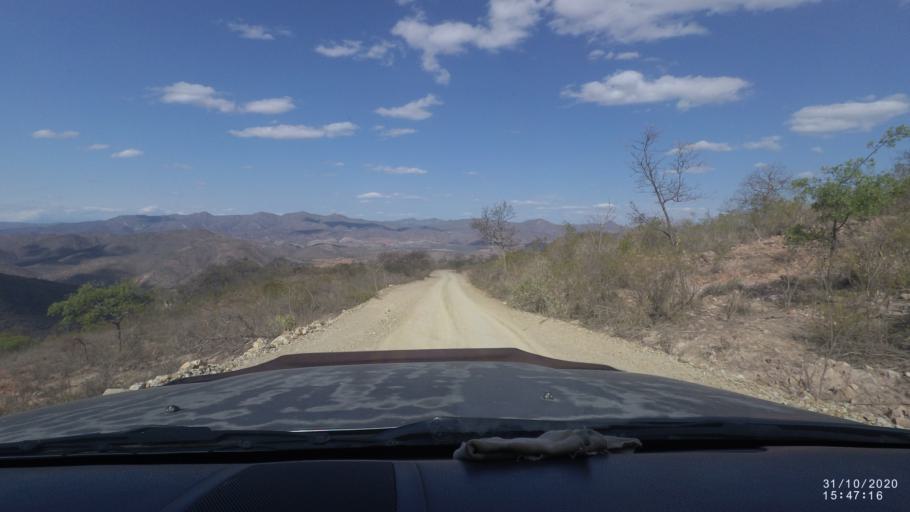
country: BO
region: Chuquisaca
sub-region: Provincia Zudanez
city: Mojocoya
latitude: -18.3139
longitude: -64.7157
